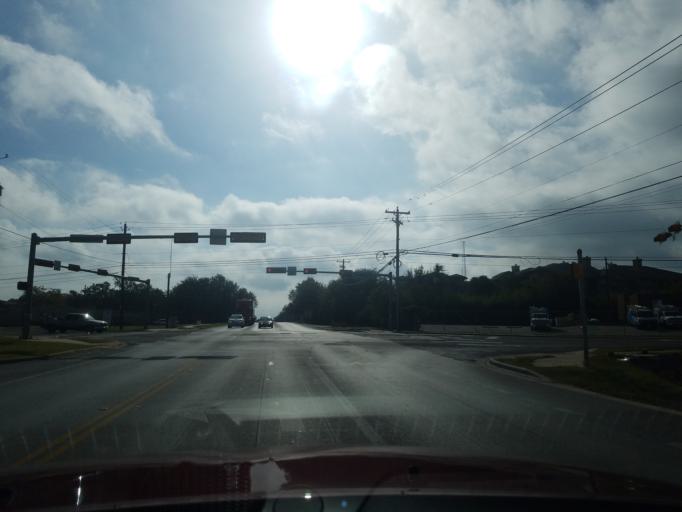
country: US
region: Texas
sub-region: Williamson County
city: Jollyville
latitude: 30.4506
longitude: -97.7856
